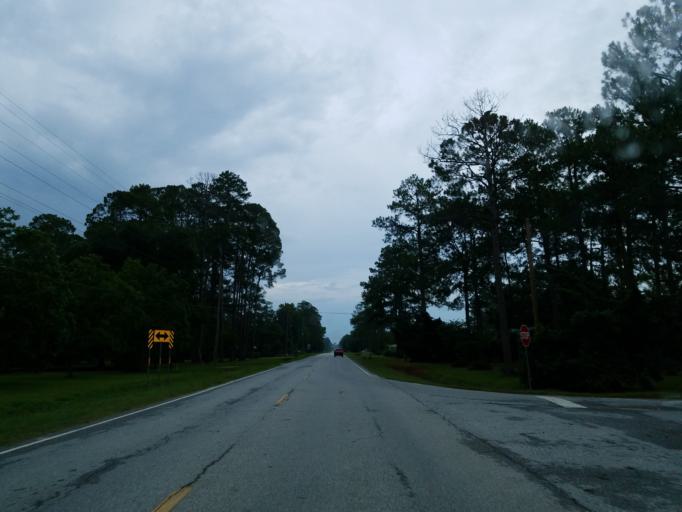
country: US
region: Georgia
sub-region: Lanier County
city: Lakeland
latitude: 31.0483
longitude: -83.1192
